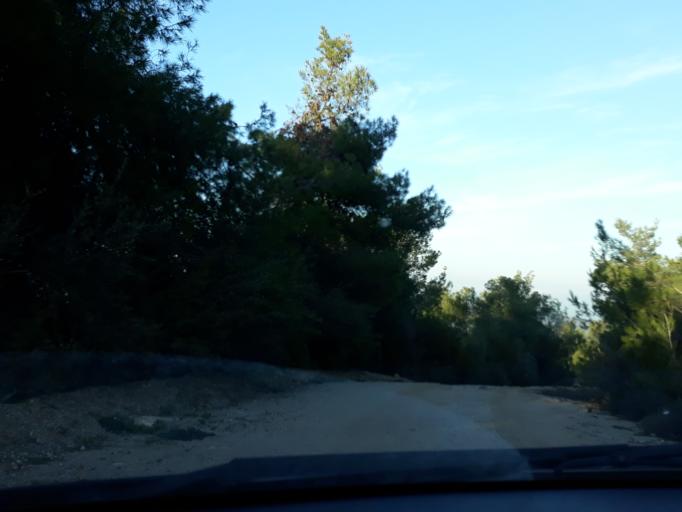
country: GR
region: Central Greece
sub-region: Nomos Voiotias
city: Asopia
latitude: 38.2731
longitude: 23.5329
